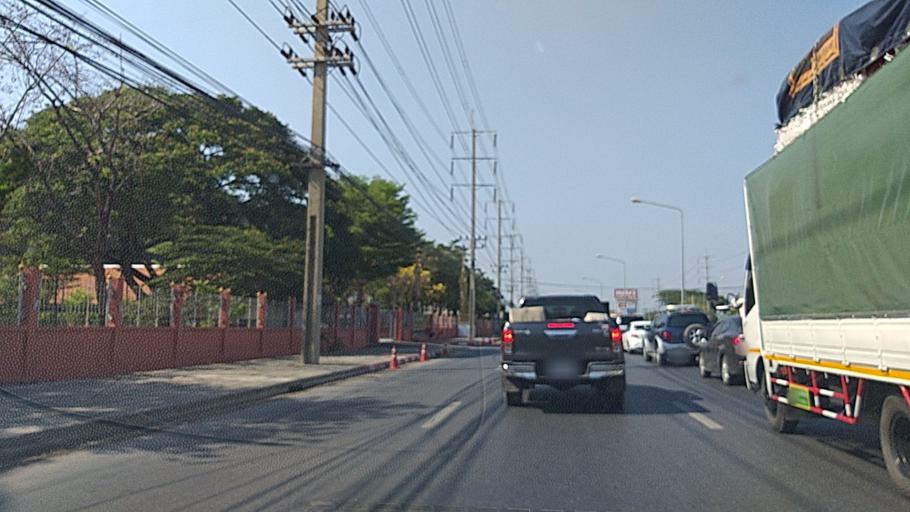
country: TH
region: Nakhon Pathom
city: Salaya
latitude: 13.7973
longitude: 100.3034
